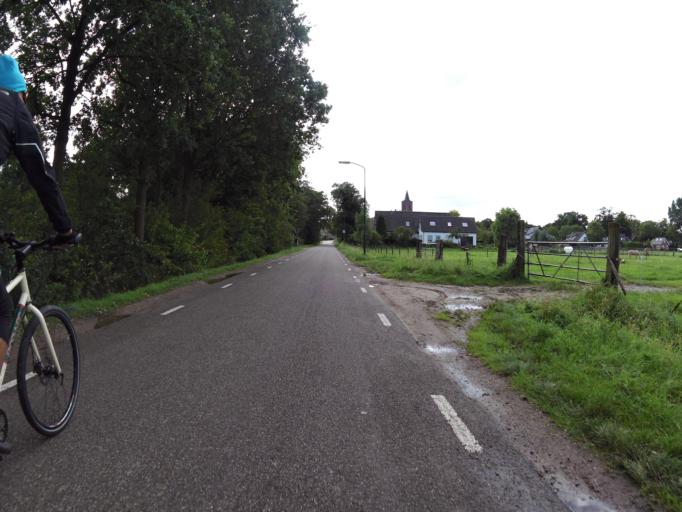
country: NL
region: Utrecht
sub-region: Gemeente Soest
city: Soest
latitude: 52.1765
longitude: 5.3167
